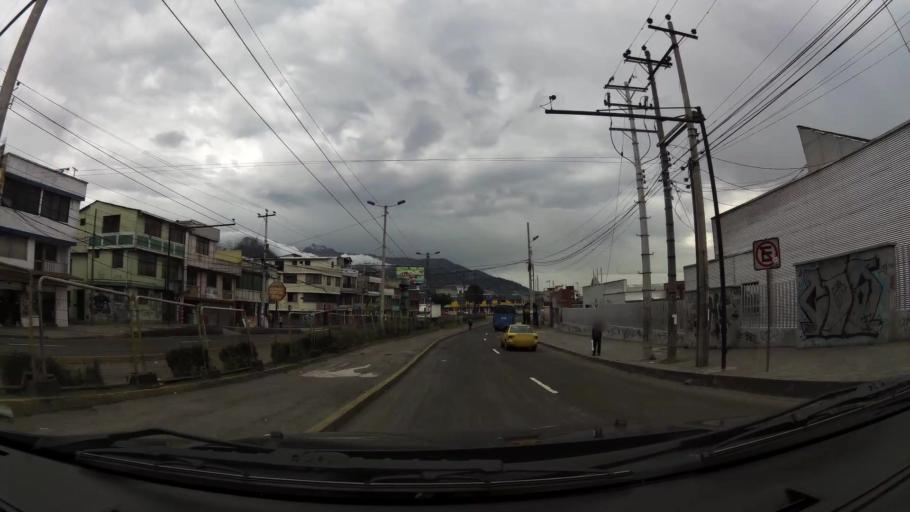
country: EC
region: Pichincha
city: Quito
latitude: -0.2782
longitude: -78.5427
